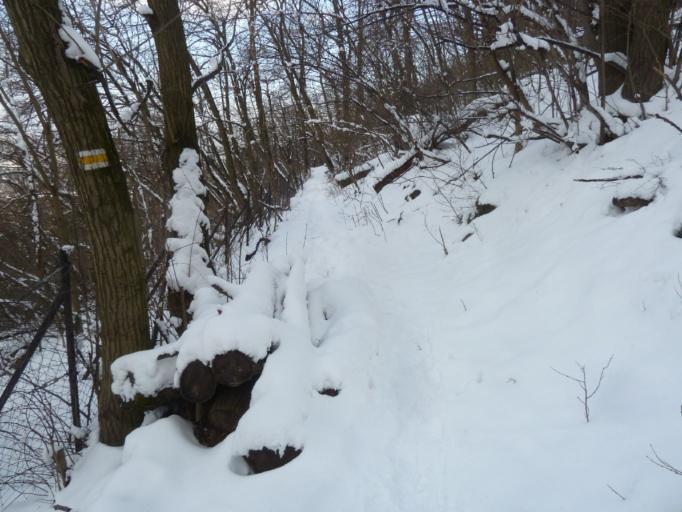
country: HU
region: Pest
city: Pilisborosjeno
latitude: 47.5714
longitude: 18.9863
